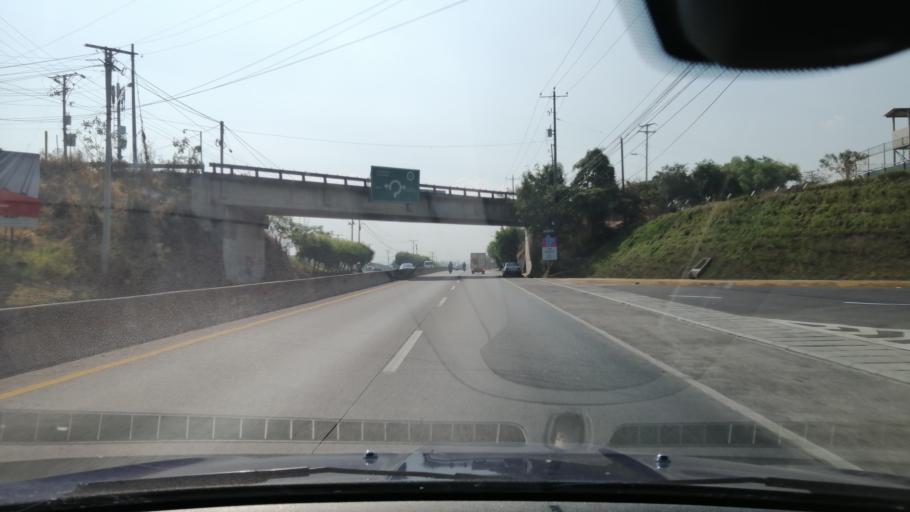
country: SV
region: San Salvador
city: Apopa
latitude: 13.7976
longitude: -89.2294
